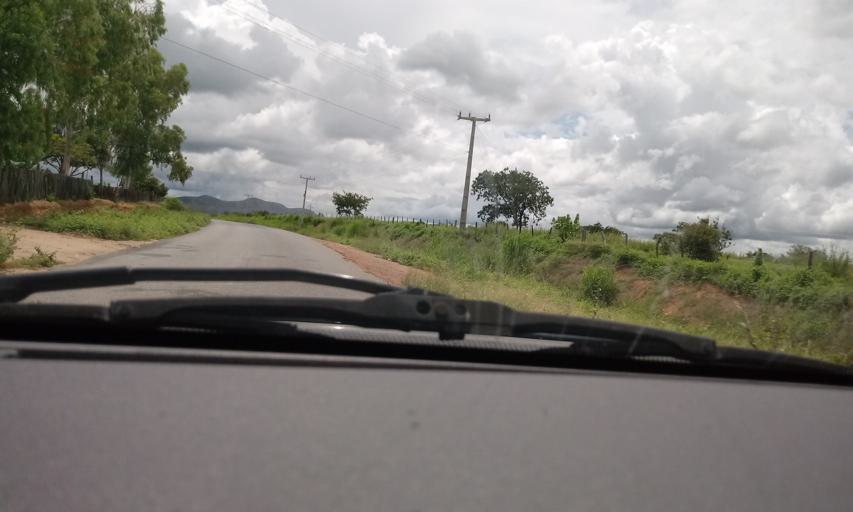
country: BR
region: Bahia
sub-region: Guanambi
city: Guanambi
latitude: -14.1775
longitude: -42.8001
